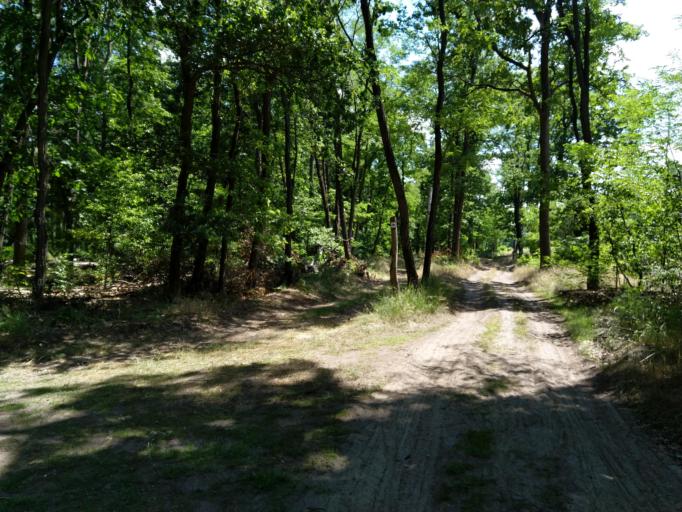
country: DE
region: Berlin
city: Friedrichshagen
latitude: 52.4555
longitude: 13.6533
